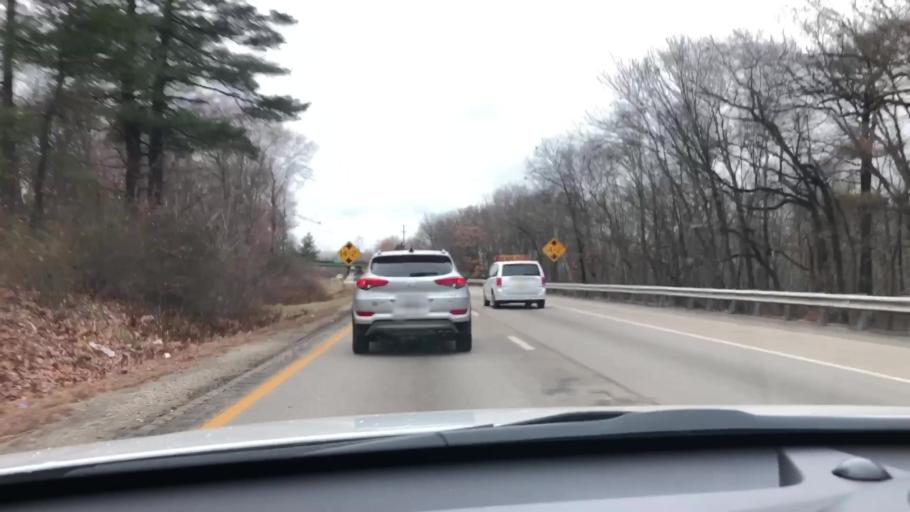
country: US
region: Massachusetts
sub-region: Norfolk County
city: Weymouth
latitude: 42.1921
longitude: -70.9470
